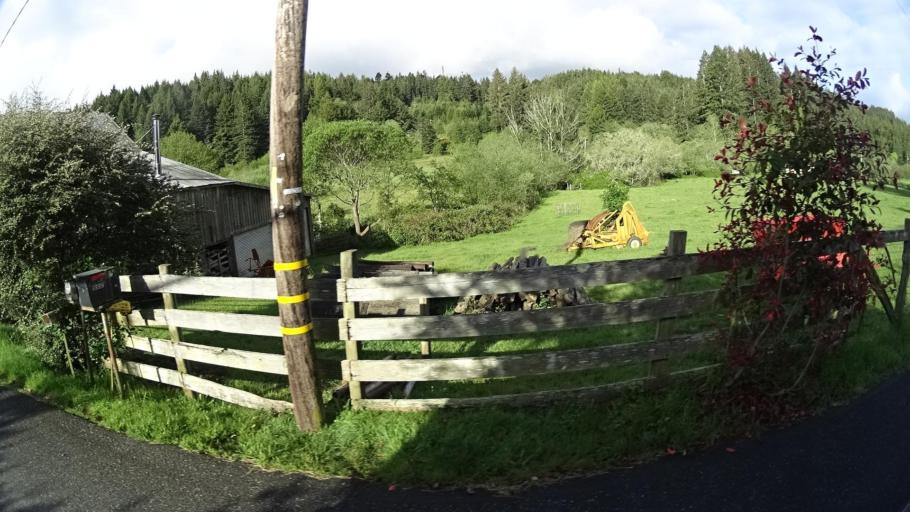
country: US
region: California
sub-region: Humboldt County
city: Arcata
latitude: 40.8931
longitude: -124.0416
